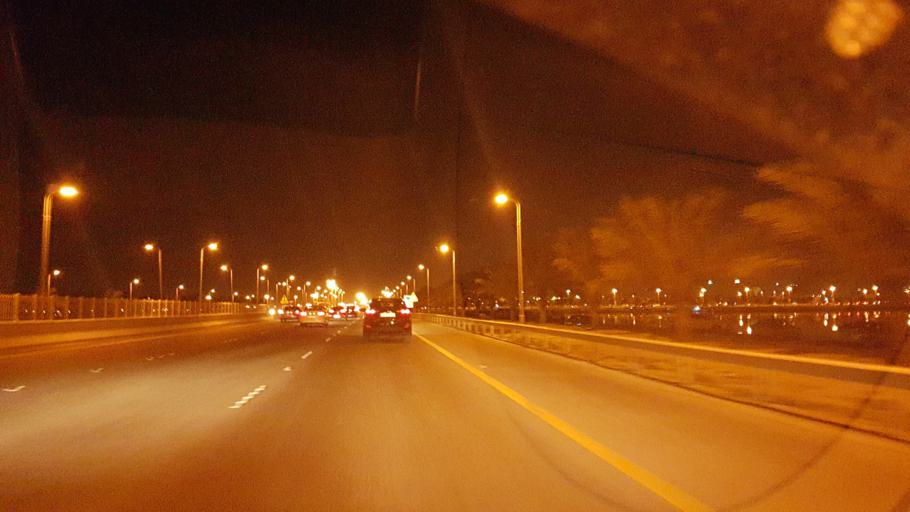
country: BH
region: Muharraq
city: Al Hadd
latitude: 26.2590
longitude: 50.6604
